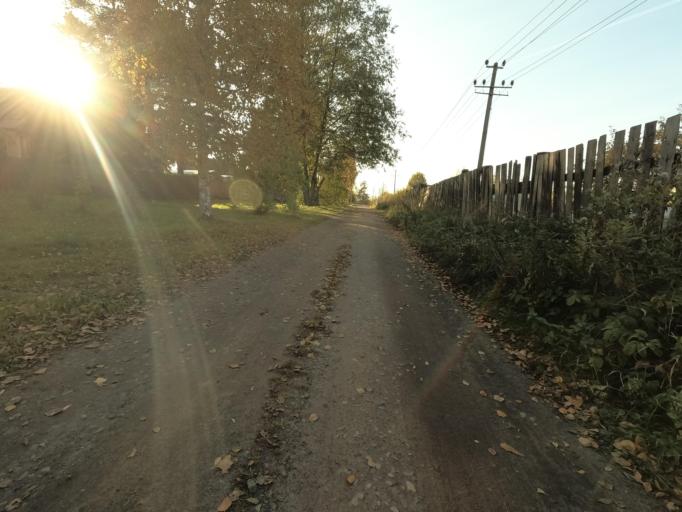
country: RU
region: Leningrad
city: Mga
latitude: 59.7562
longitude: 31.0475
